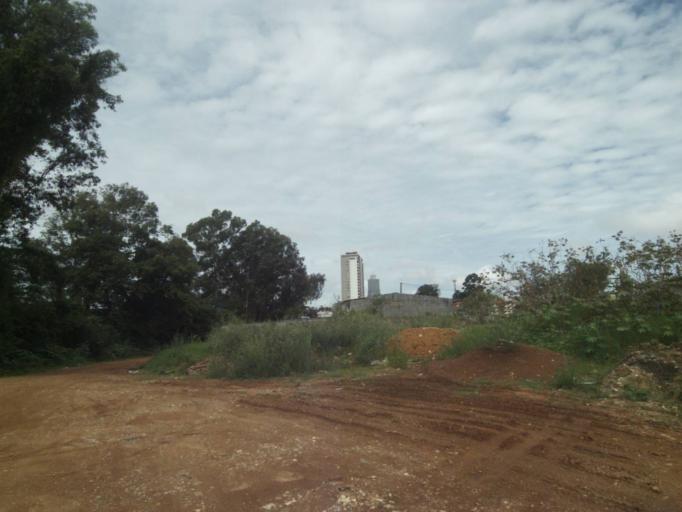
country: BR
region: Parana
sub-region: Curitiba
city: Curitiba
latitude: -25.4382
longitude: -49.3162
